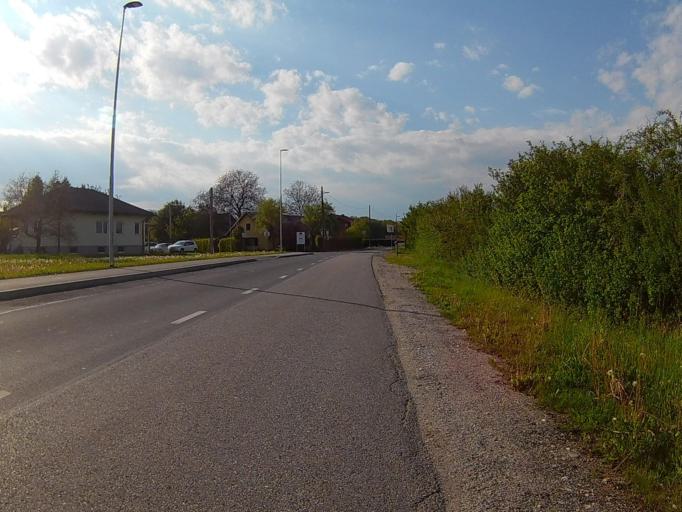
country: SI
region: Race-Fram
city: Race
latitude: 46.4671
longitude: 15.7140
